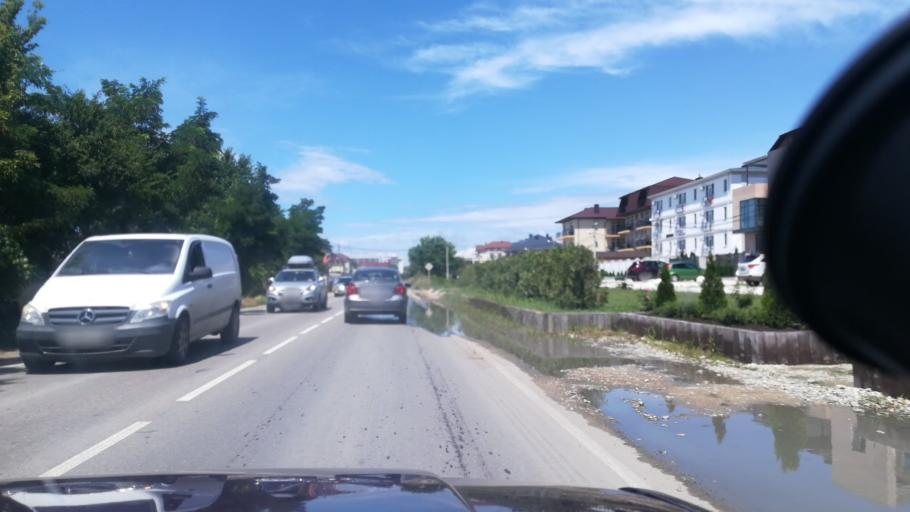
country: RU
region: Krasnodarskiy
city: Vityazevo
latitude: 44.9597
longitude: 37.2958
